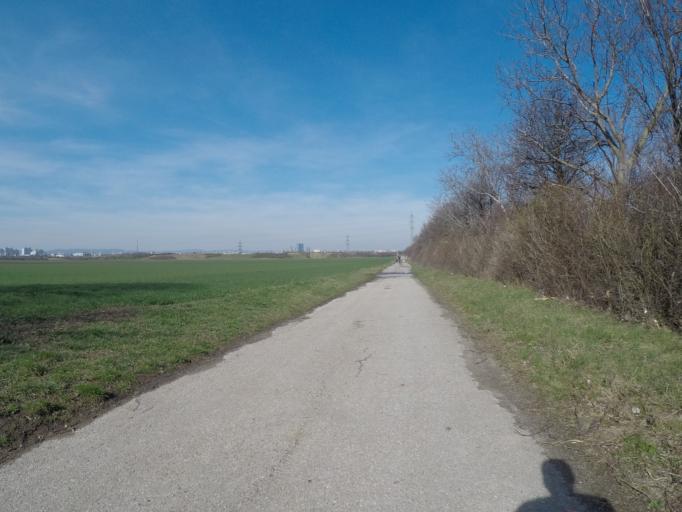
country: AT
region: Lower Austria
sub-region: Politischer Bezirk Modling
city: Vosendorf
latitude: 48.1264
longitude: 16.3433
